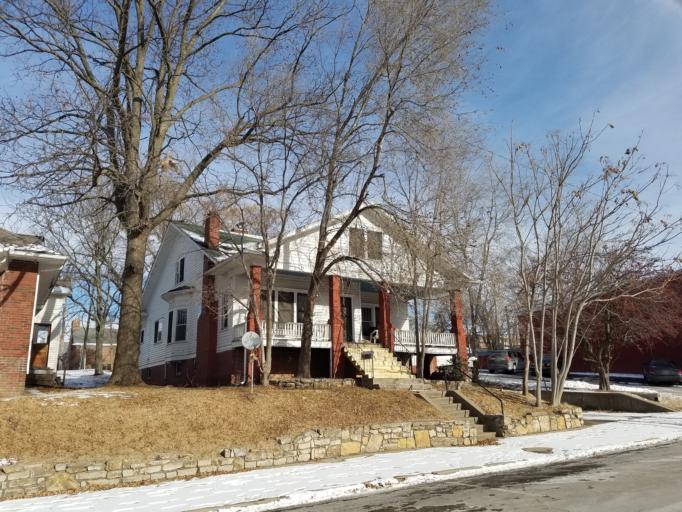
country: US
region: Missouri
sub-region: Lafayette County
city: Lexington
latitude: 39.1845
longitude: -93.8807
